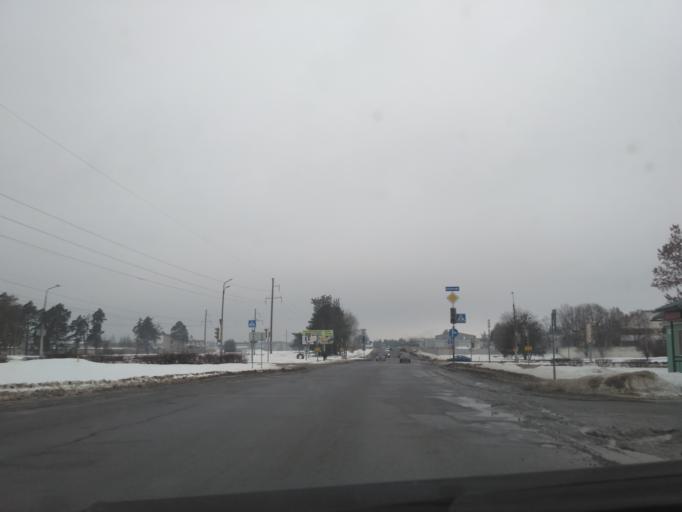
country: BY
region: Minsk
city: Horad Barysaw
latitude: 54.1989
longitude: 28.4974
